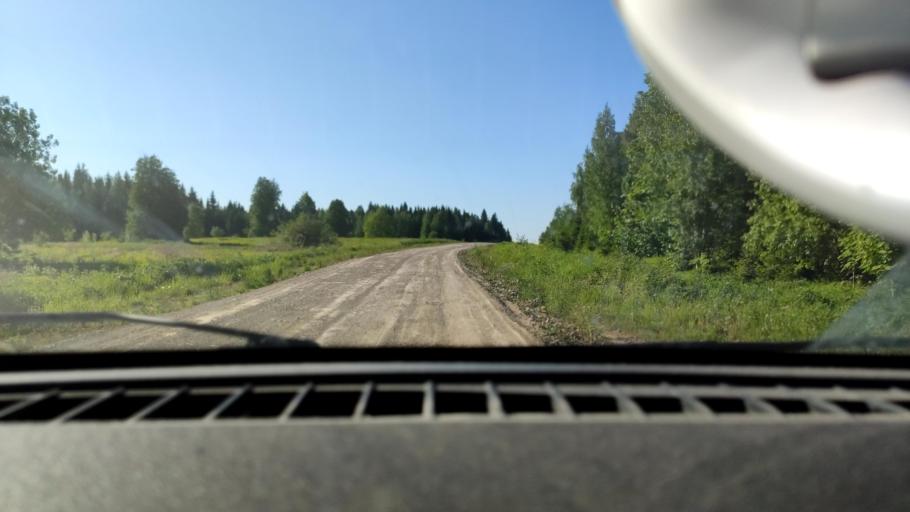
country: RU
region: Perm
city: Novyye Lyady
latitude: 58.1811
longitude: 56.5881
